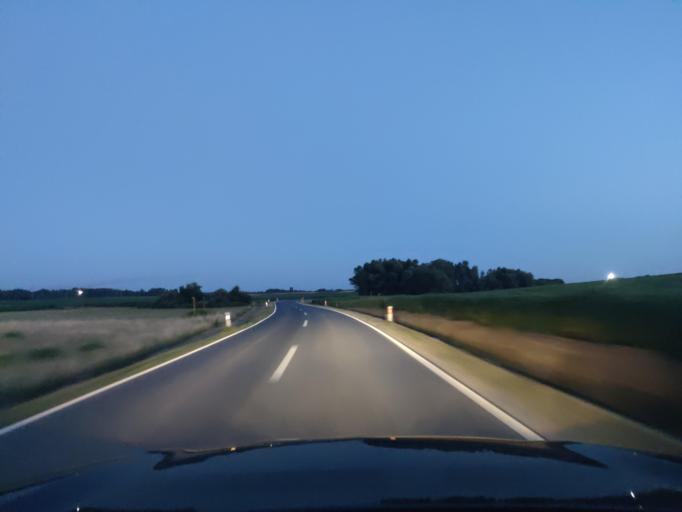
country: HR
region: Medimurska
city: Vratisinec
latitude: 46.4882
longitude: 16.4256
